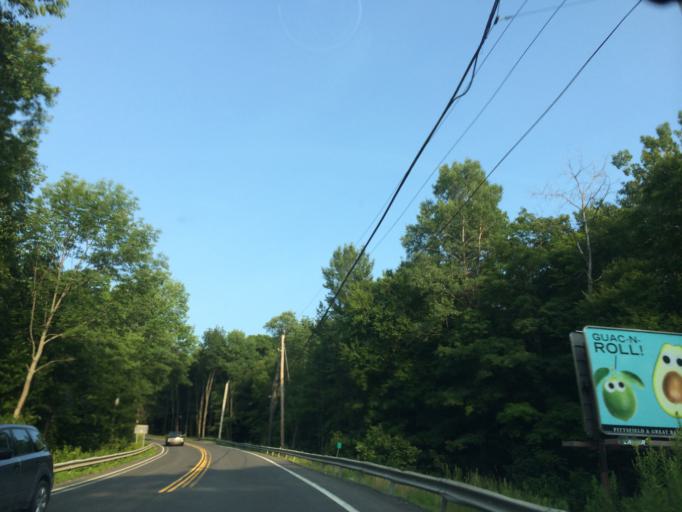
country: US
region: Massachusetts
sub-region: Berkshire County
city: Richmond
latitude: 42.3901
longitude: -73.4035
